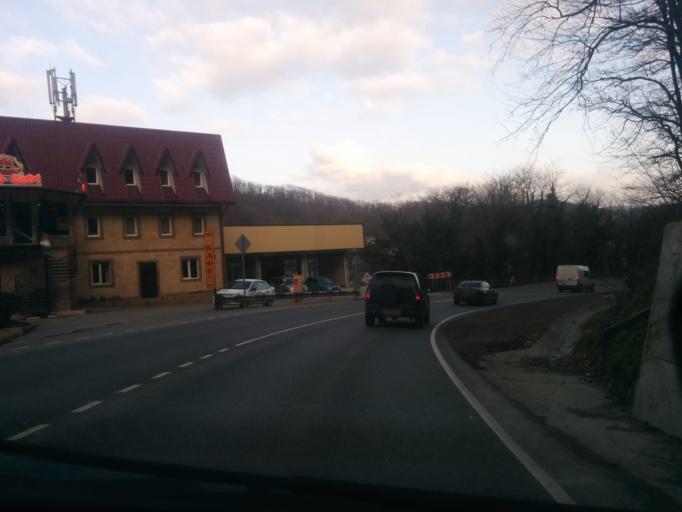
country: RU
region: Krasnodarskiy
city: Tuapse
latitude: 44.1178
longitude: 39.0527
